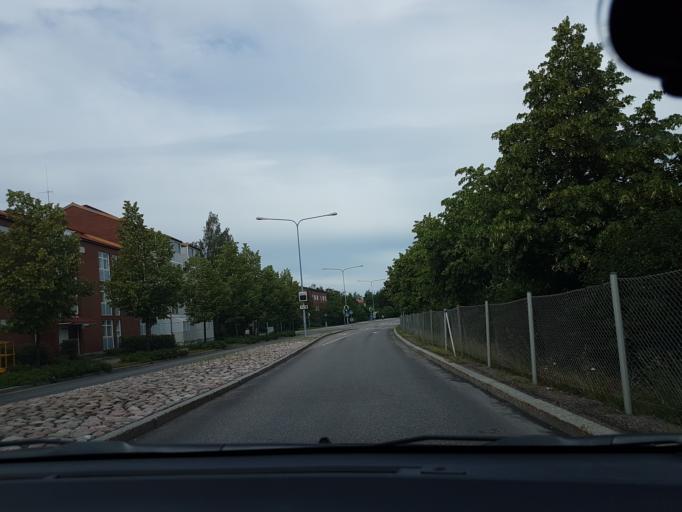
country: FI
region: Uusimaa
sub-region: Helsinki
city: Vantaa
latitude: 60.2561
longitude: 25.0139
